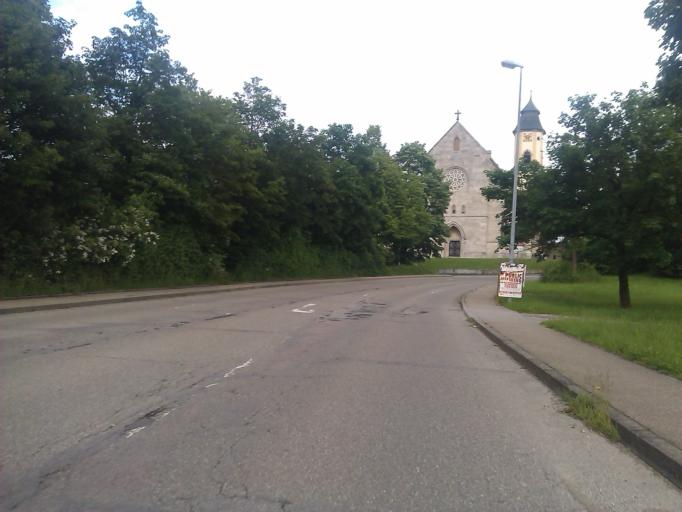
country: DE
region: Baden-Wuerttemberg
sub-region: Regierungsbezirk Stuttgart
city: Abtsgmund
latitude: 48.8952
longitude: 10.0006
